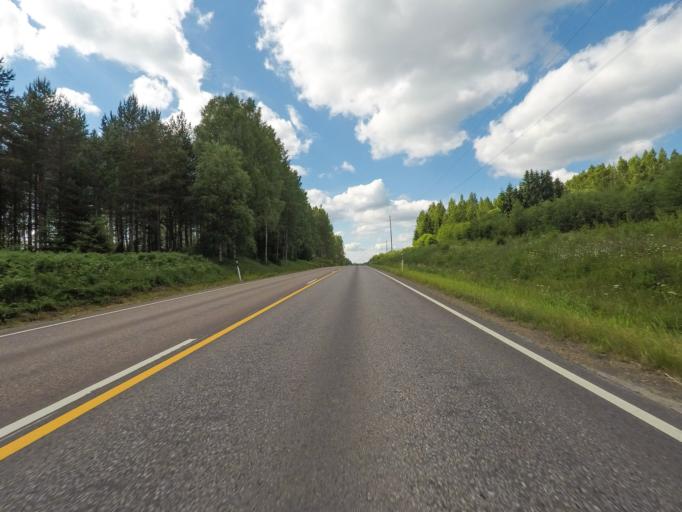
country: FI
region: Southern Savonia
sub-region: Savonlinna
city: Kerimaeki
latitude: 61.8527
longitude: 29.1697
